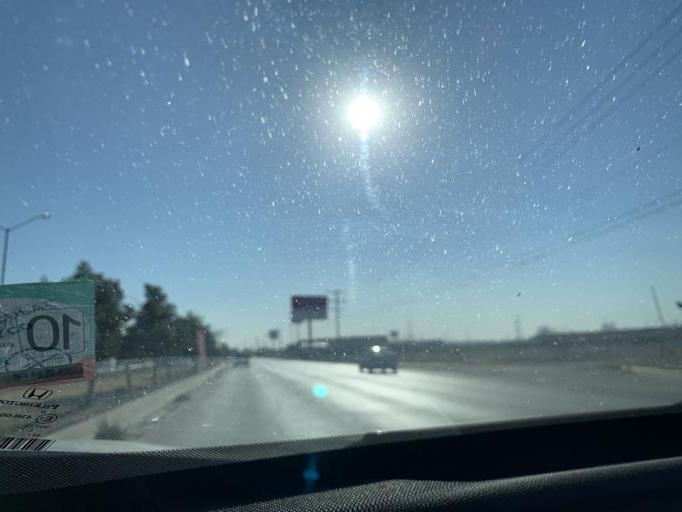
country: US
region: Texas
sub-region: El Paso County
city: Socorro
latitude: 31.6813
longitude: -106.3919
